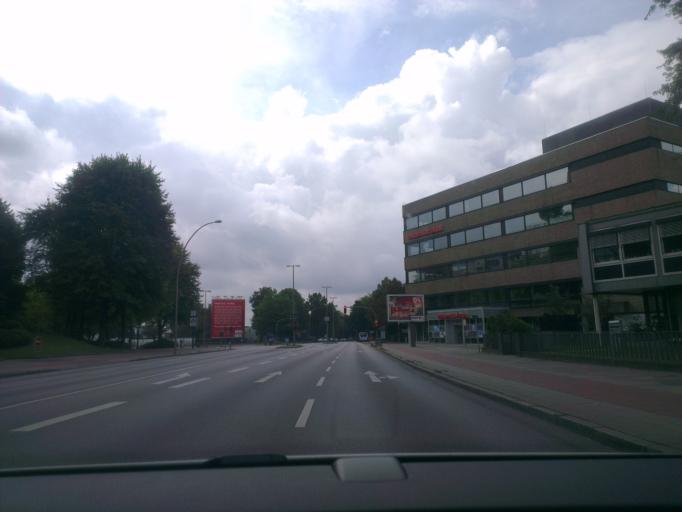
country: DE
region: Hamburg
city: Steilshoop
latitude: 53.6022
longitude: 10.0693
